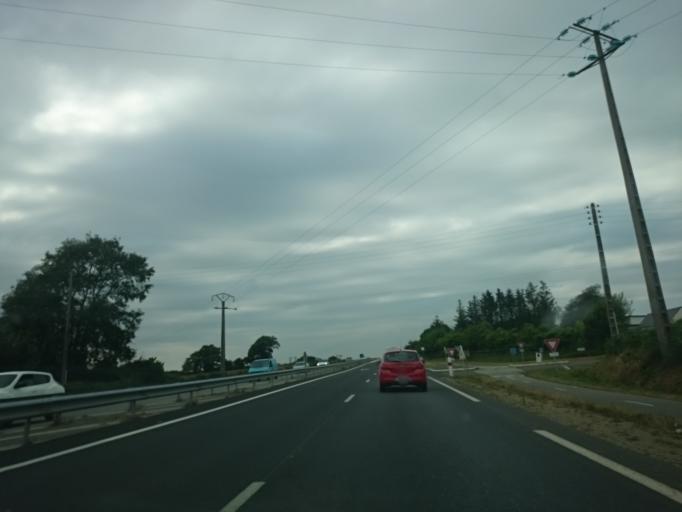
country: FR
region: Brittany
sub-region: Departement du Finistere
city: Guilers
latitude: 48.4175
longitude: -4.5474
